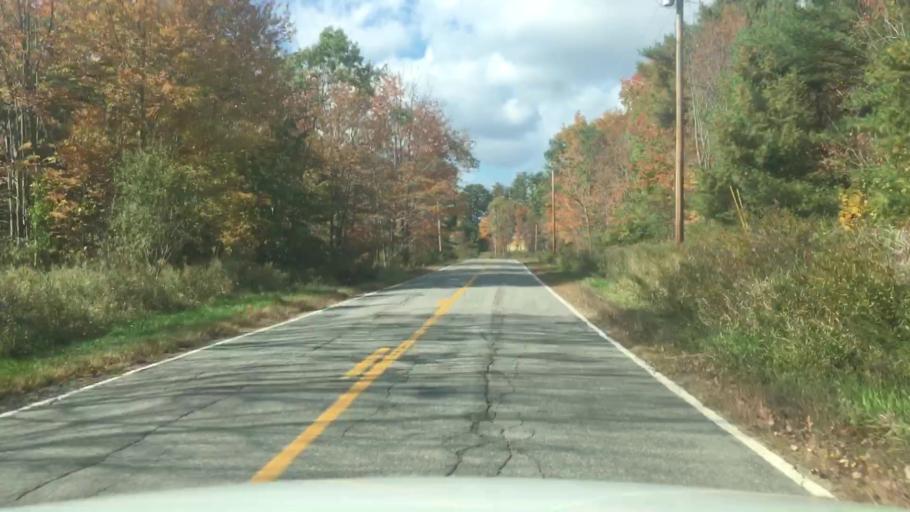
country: US
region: Maine
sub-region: Knox County
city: Washington
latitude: 44.3043
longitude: -69.3334
